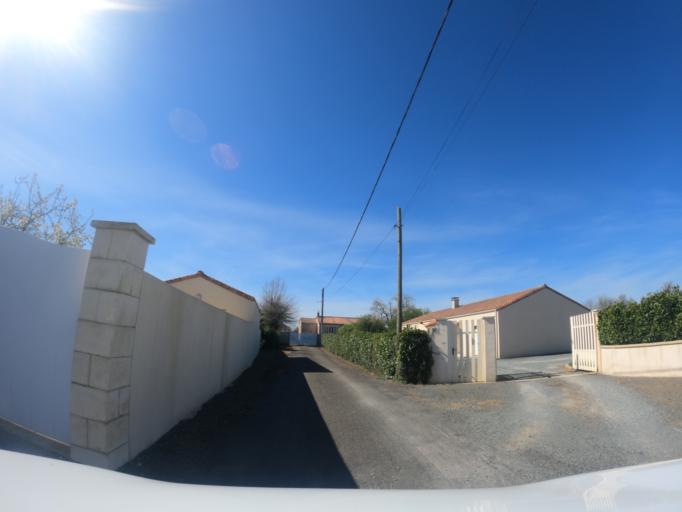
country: FR
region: Pays de la Loire
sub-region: Departement de la Vendee
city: Saint-Pierre-du-Chemin
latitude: 46.6952
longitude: -0.7050
